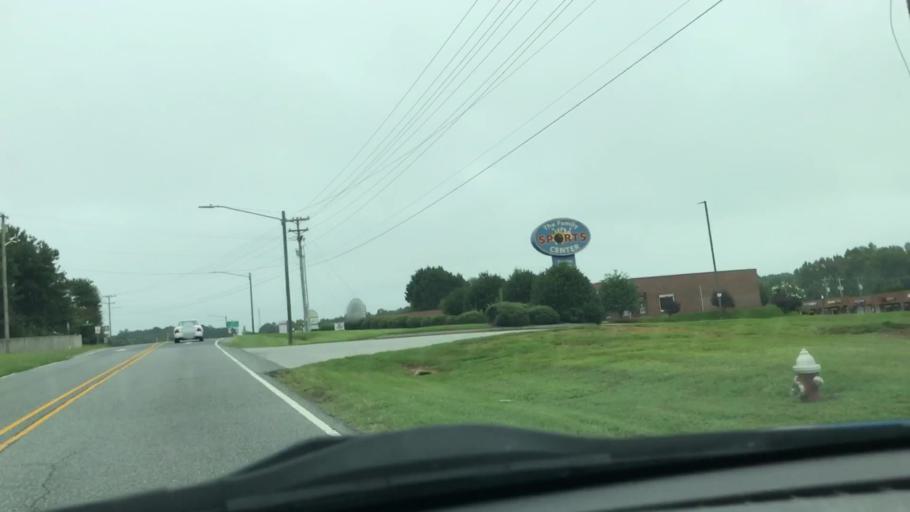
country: US
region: North Carolina
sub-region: Randolph County
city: Asheboro
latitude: 35.7002
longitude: -79.7913
